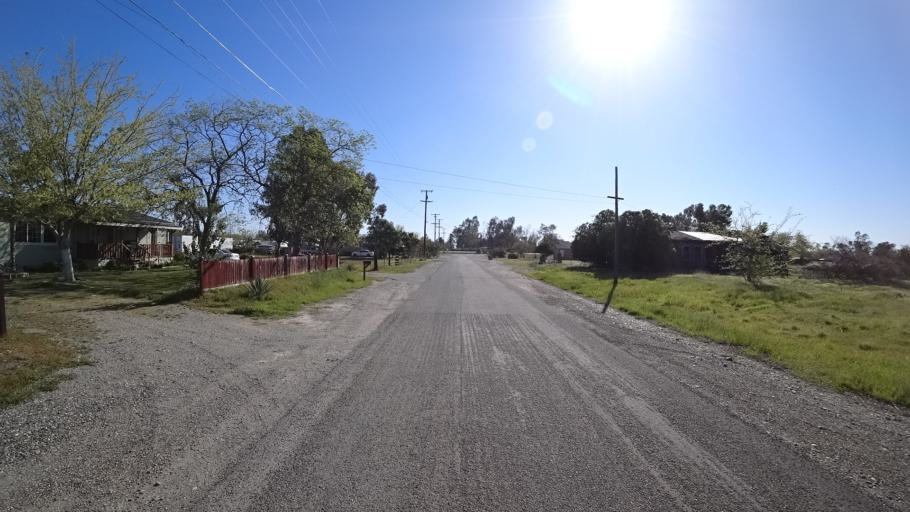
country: US
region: California
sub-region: Glenn County
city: Orland
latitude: 39.7439
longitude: -122.2080
